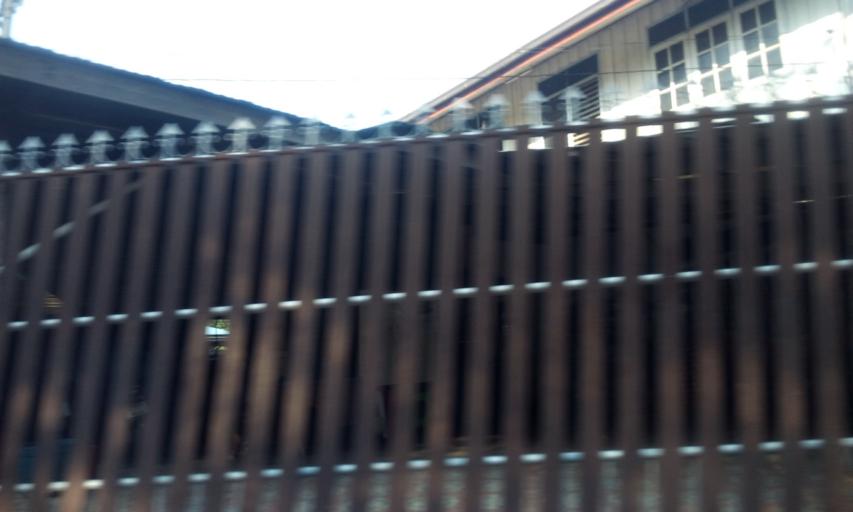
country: TH
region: Sing Buri
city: Sing Buri
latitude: 14.8516
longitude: 100.3898
